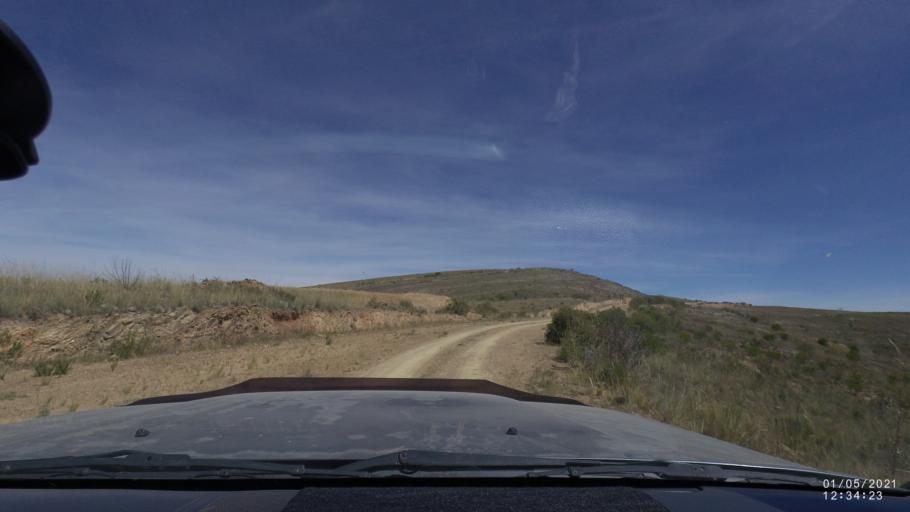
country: BO
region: Cochabamba
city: Capinota
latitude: -17.6766
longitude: -66.1505
